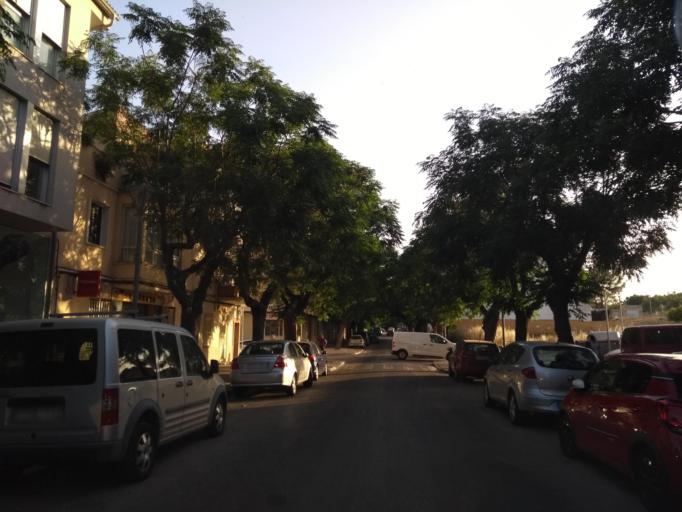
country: ES
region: Balearic Islands
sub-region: Illes Balears
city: Inca
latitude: 39.7255
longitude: 2.9201
